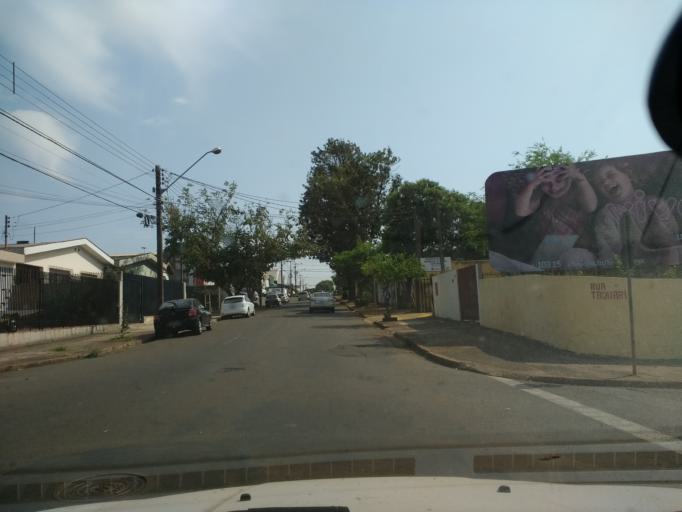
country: BR
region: Parana
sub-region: Londrina
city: Londrina
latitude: -23.2973
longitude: -51.1615
